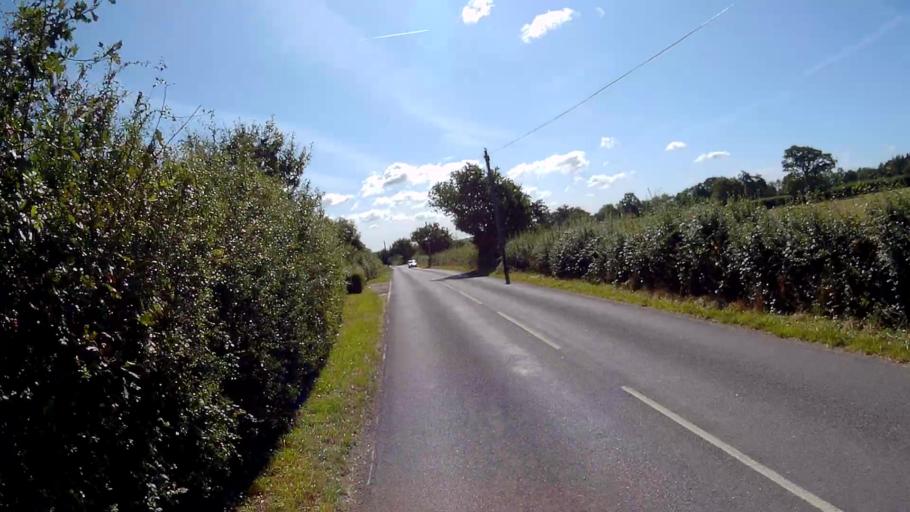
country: GB
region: England
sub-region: West Berkshire
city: Stratfield Mortimer
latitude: 51.3689
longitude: -1.0282
